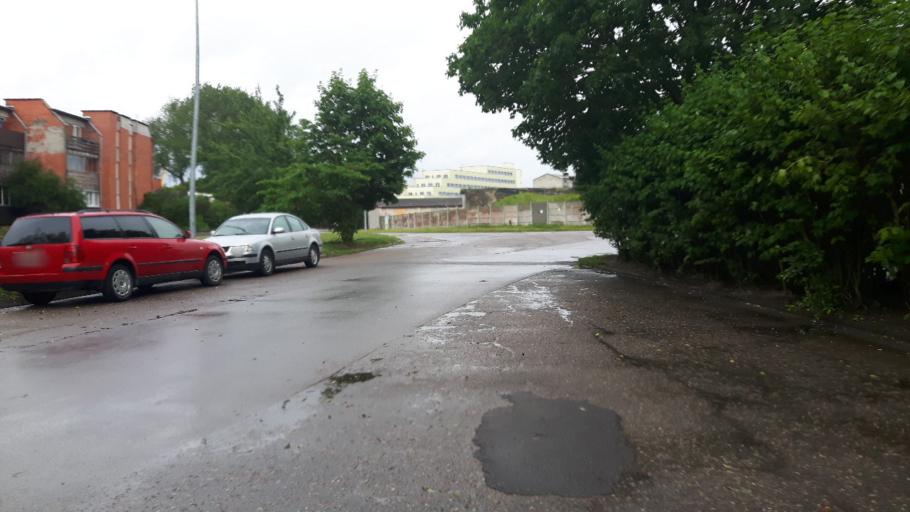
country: LV
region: Liepaja
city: Liepaja
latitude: 56.5143
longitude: 20.9903
